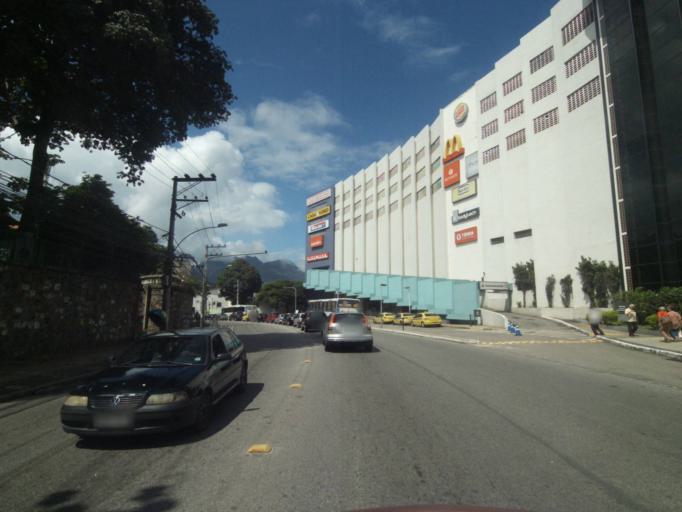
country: BR
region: Rio de Janeiro
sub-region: Sao Joao De Meriti
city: Sao Joao de Meriti
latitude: -22.9246
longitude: -43.3611
